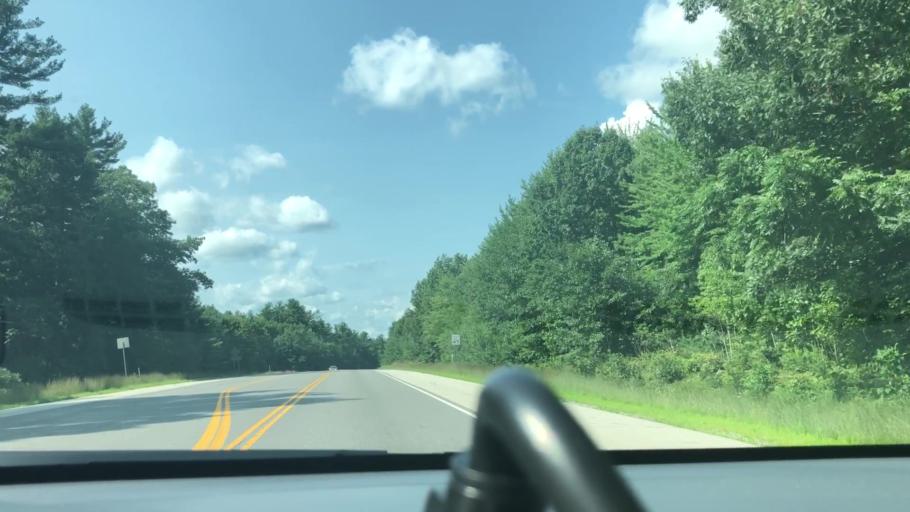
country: US
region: New Hampshire
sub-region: Hillsborough County
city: Pinardville
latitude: 42.9912
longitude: -71.5241
